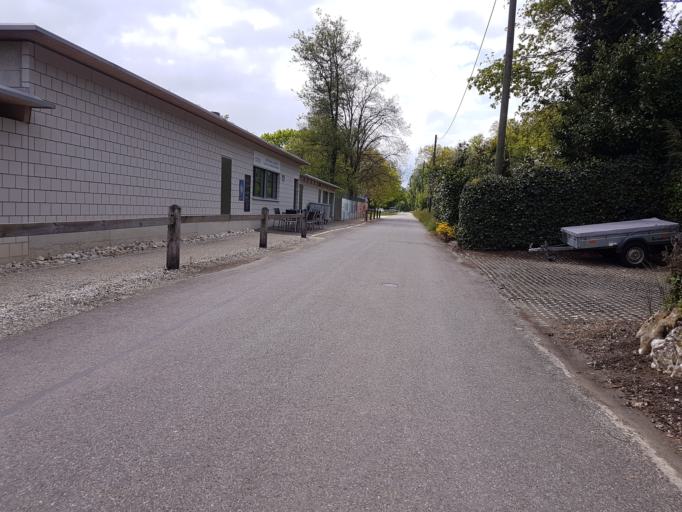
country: CH
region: Aargau
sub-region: Bezirk Brugg
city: Rupperswil
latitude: 47.4129
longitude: 8.1205
